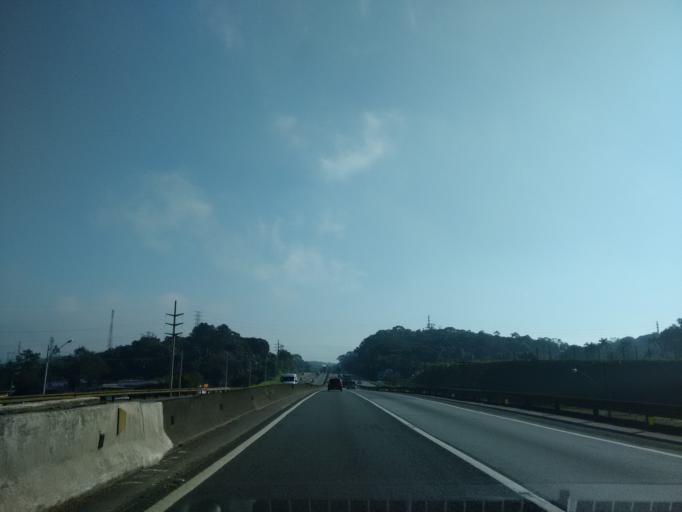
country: BR
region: Santa Catarina
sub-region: Joinville
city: Joinville
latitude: -26.2960
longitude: -48.8841
